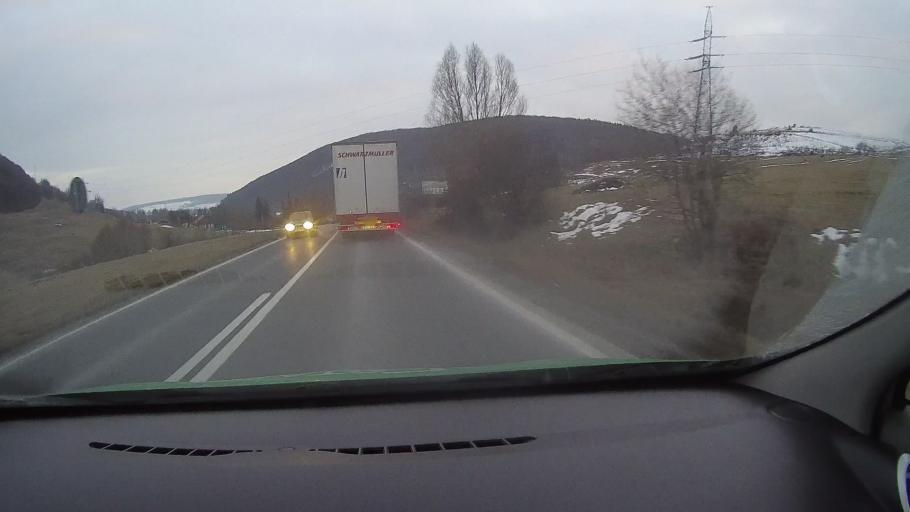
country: RO
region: Harghita
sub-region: Municipiul Odorheiu Secuiesc
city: Odorheiu Secuiesc
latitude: 46.3383
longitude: 25.2698
